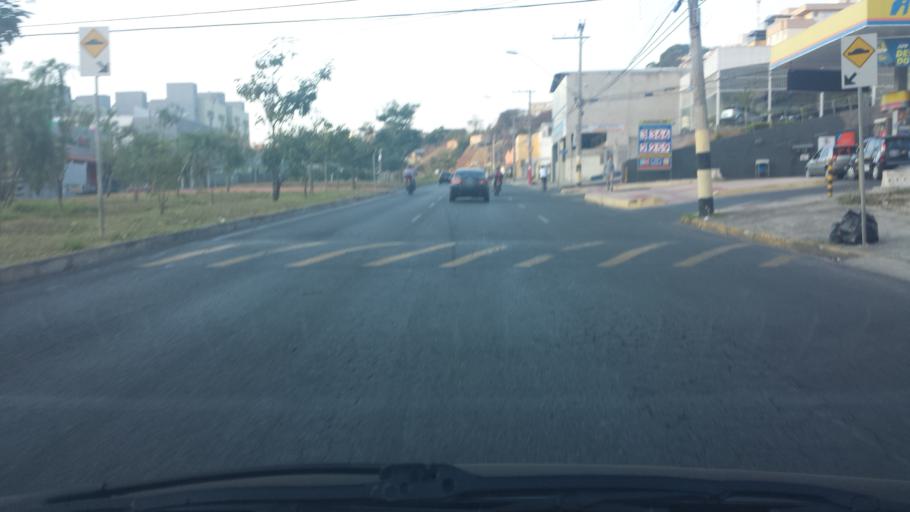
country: BR
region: Minas Gerais
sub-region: Belo Horizonte
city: Belo Horizonte
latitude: -19.8905
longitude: -43.9934
